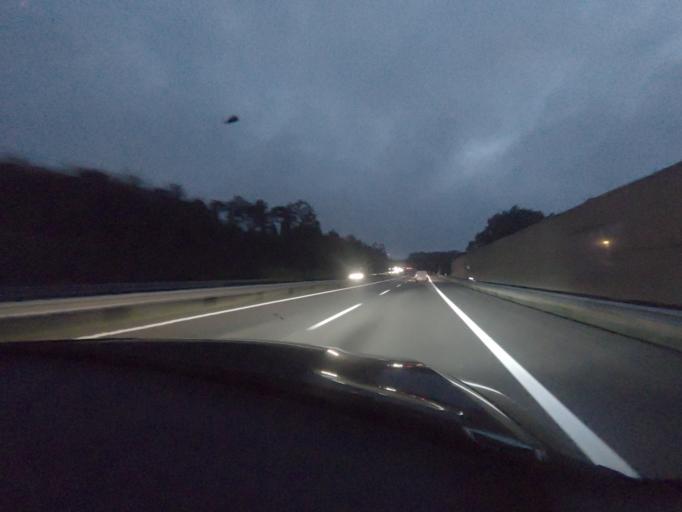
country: PT
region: Leiria
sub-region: Leiria
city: Caranguejeira
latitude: 39.8035
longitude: -8.7240
